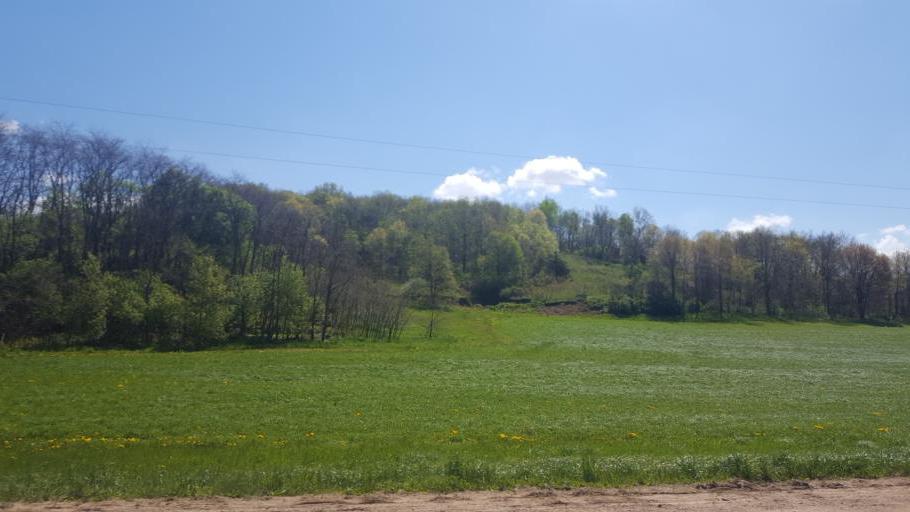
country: US
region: Wisconsin
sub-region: Vernon County
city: Hillsboro
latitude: 43.6279
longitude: -90.3581
